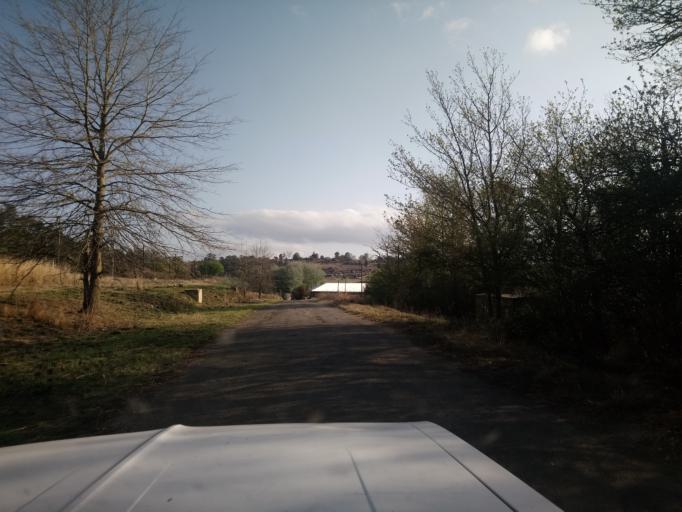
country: ZA
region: KwaZulu-Natal
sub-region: uMgungundlovu District Municipality
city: Mooirivier
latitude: -29.3059
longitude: 29.9780
